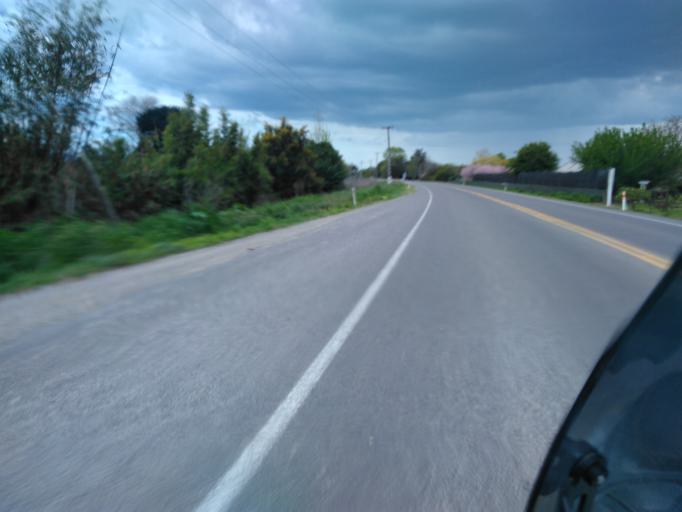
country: NZ
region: Gisborne
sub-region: Gisborne District
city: Gisborne
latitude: -38.6558
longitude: 177.9220
